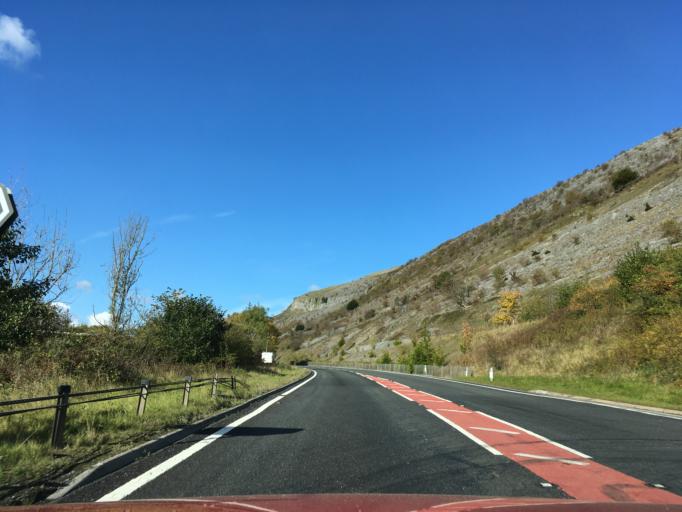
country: GB
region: Wales
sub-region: Merthyr Tydfil County Borough
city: Merthyr Tydfil
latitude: 51.7725
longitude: -3.4176
